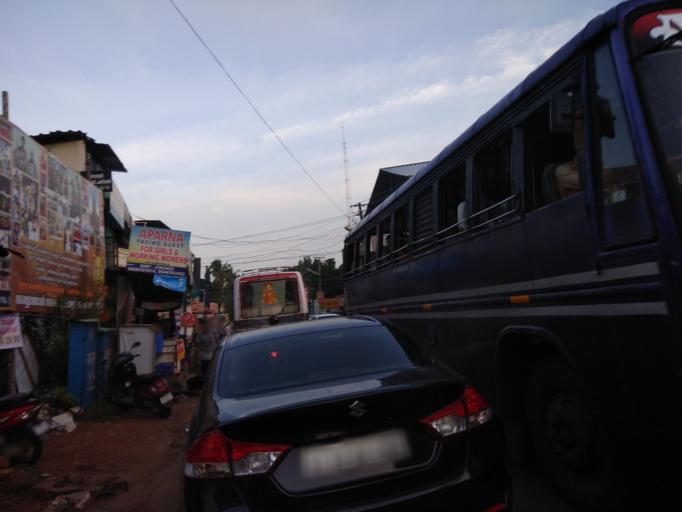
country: IN
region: Kerala
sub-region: Thrissur District
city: Trichur
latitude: 10.5278
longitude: 76.1869
